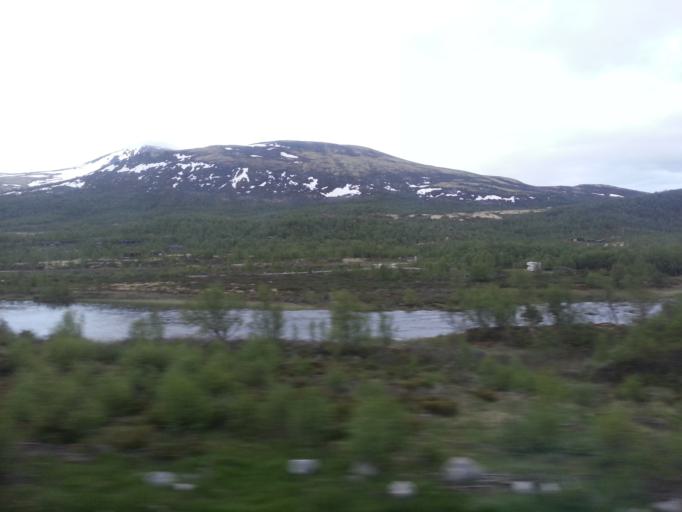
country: NO
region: Oppland
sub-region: Dovre
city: Dovre
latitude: 62.1761
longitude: 9.4263
